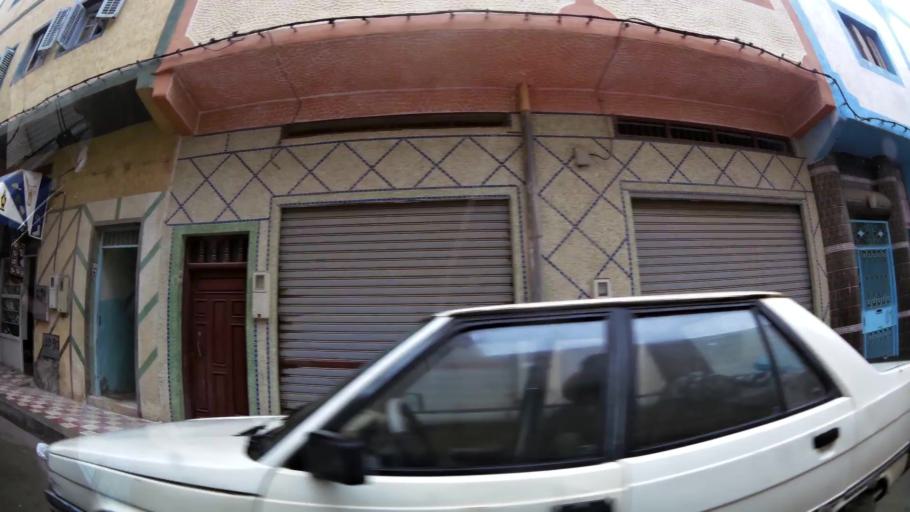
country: MA
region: Taza-Al Hoceima-Taounate
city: Imzourene
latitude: 35.1447
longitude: -3.8505
